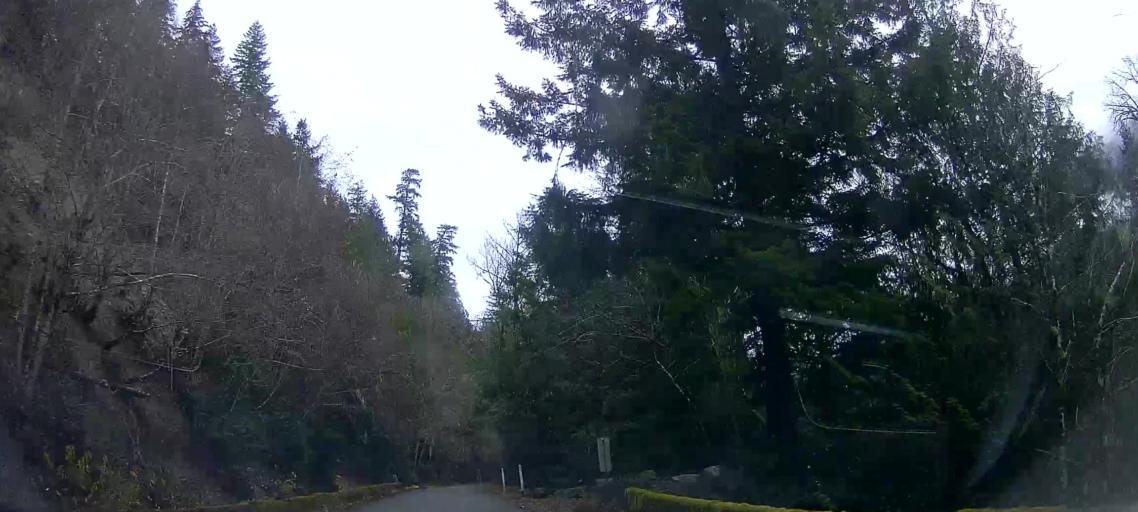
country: US
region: Washington
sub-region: Snohomish County
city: Darrington
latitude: 48.5225
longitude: -121.3753
